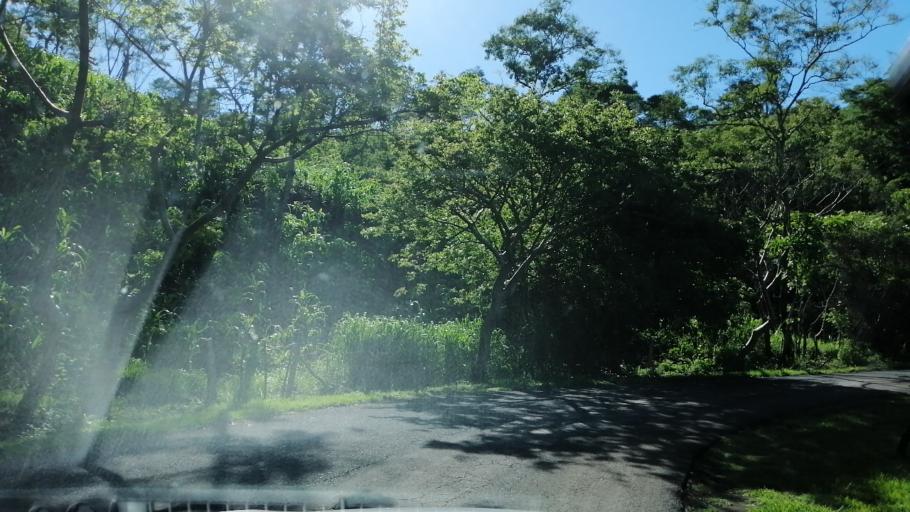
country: SV
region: Morazan
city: Corinto
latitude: 13.7962
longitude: -88.0086
